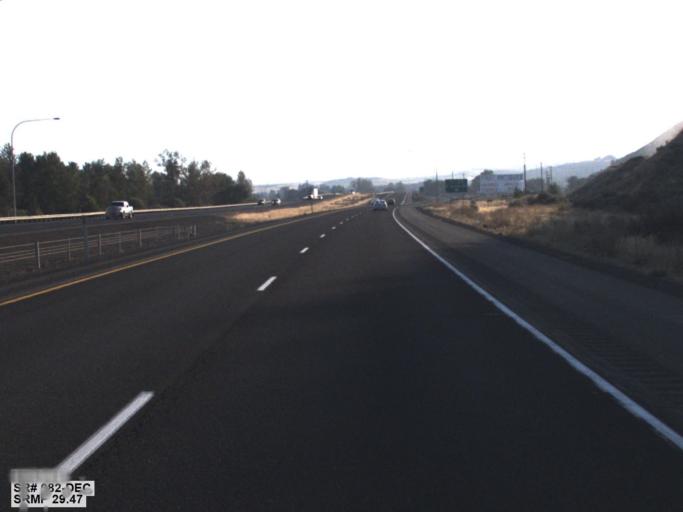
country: US
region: Washington
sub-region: Yakima County
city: Selah
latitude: 46.6443
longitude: -120.5102
